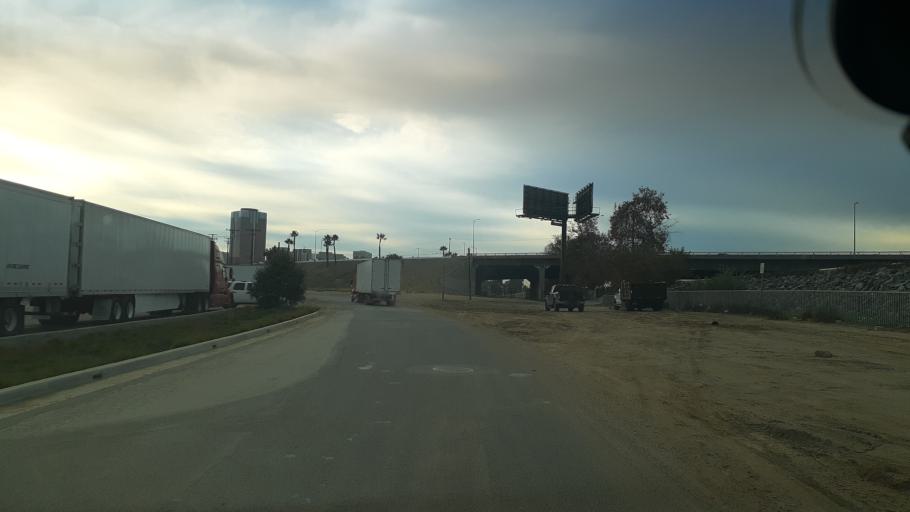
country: US
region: California
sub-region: Los Angeles County
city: Long Beach
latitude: 33.7780
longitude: -118.2042
